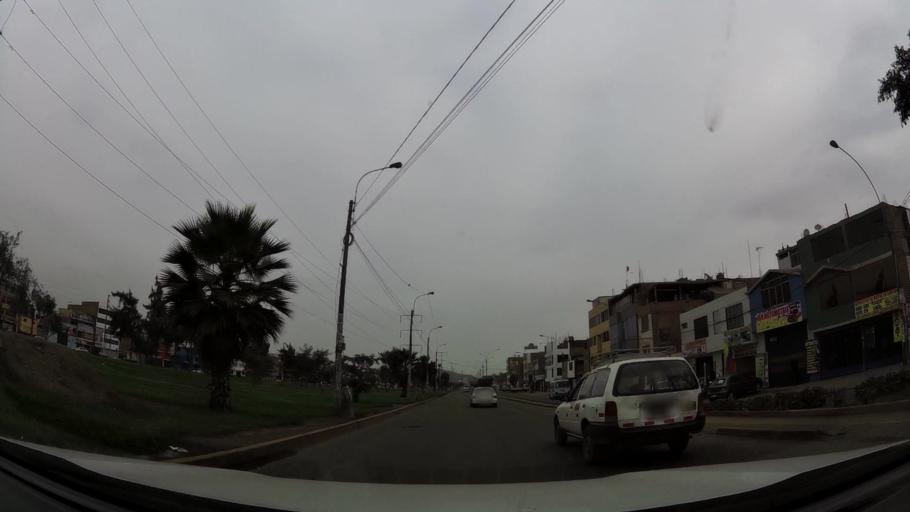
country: PE
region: Lima
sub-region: Lima
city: Independencia
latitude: -11.9783
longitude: -77.0777
